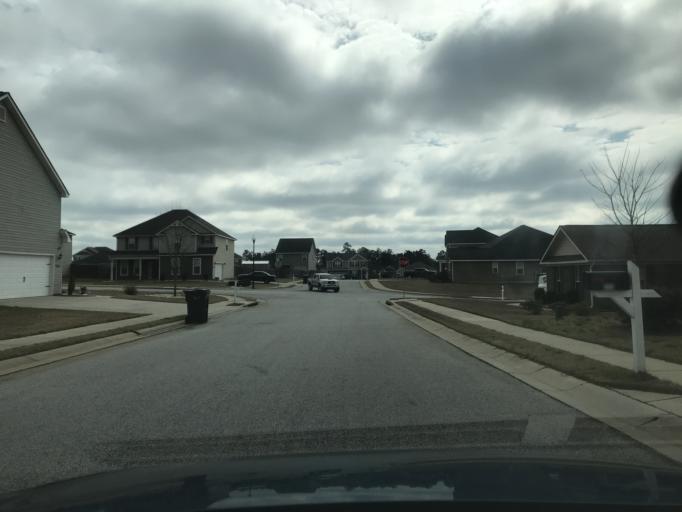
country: US
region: Georgia
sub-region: Columbia County
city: Grovetown
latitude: 33.4409
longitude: -82.1493
